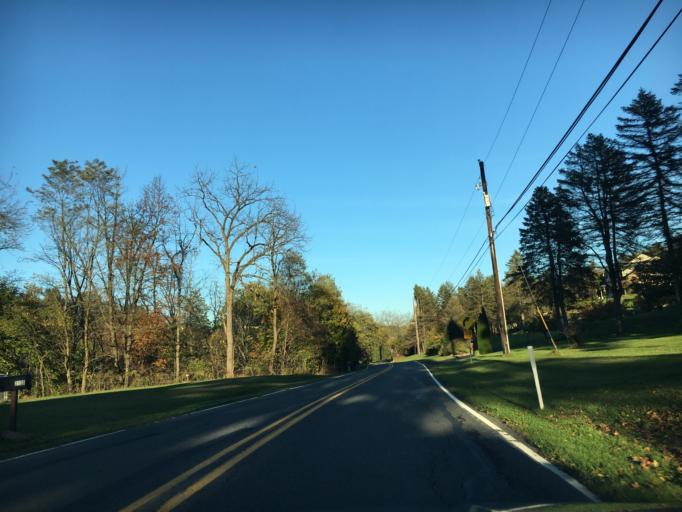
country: US
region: Pennsylvania
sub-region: Lehigh County
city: Laurys Station
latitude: 40.7049
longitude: -75.5655
